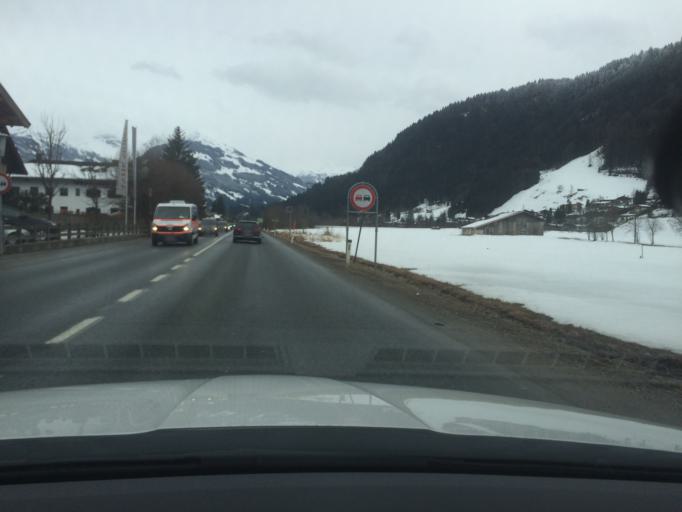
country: AT
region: Tyrol
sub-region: Politischer Bezirk Kitzbuhel
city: Kitzbuhel
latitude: 47.4342
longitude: 12.4066
